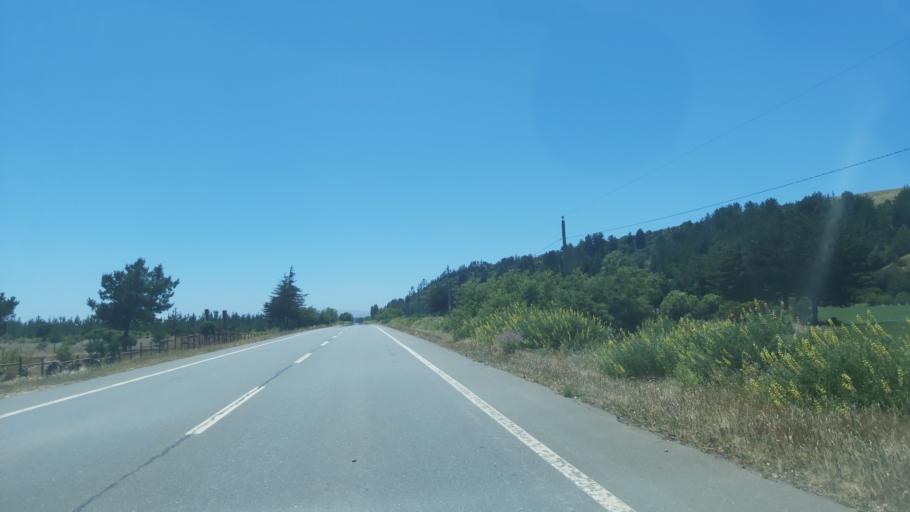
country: CL
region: Maule
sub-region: Provincia de Talca
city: Constitucion
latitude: -35.1680
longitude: -72.2636
